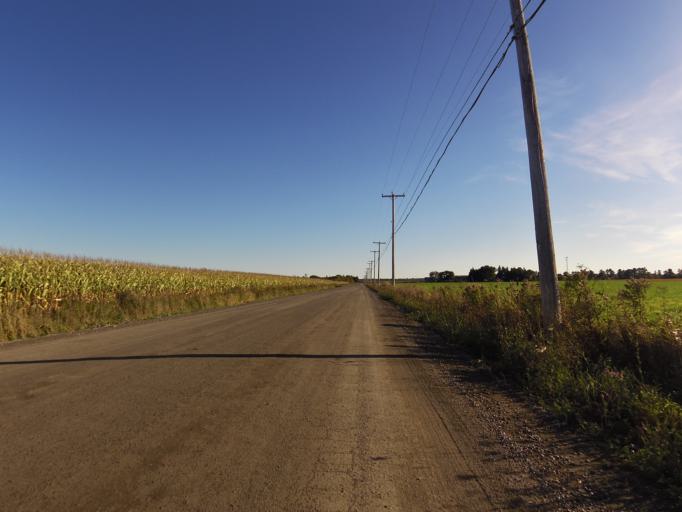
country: CA
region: Ontario
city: Bells Corners
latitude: 45.4819
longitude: -75.8808
